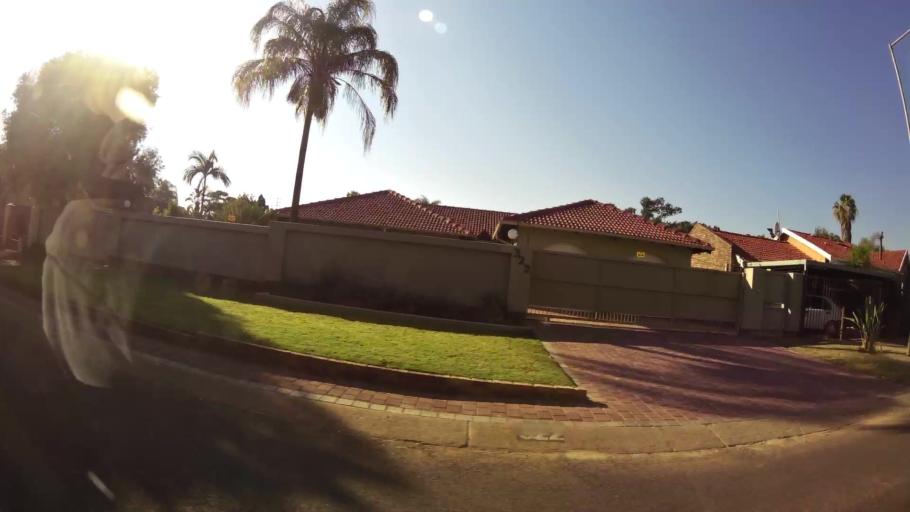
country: ZA
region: Gauteng
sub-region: City of Tshwane Metropolitan Municipality
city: Pretoria
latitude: -25.6763
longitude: 28.2332
